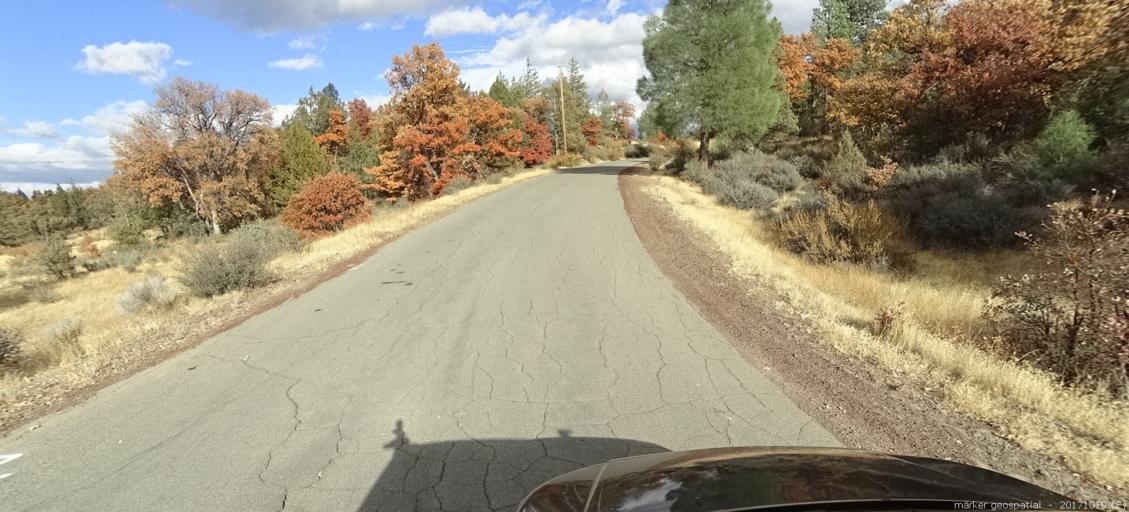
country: US
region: California
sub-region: Shasta County
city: Burney
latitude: 40.9774
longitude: -121.4454
